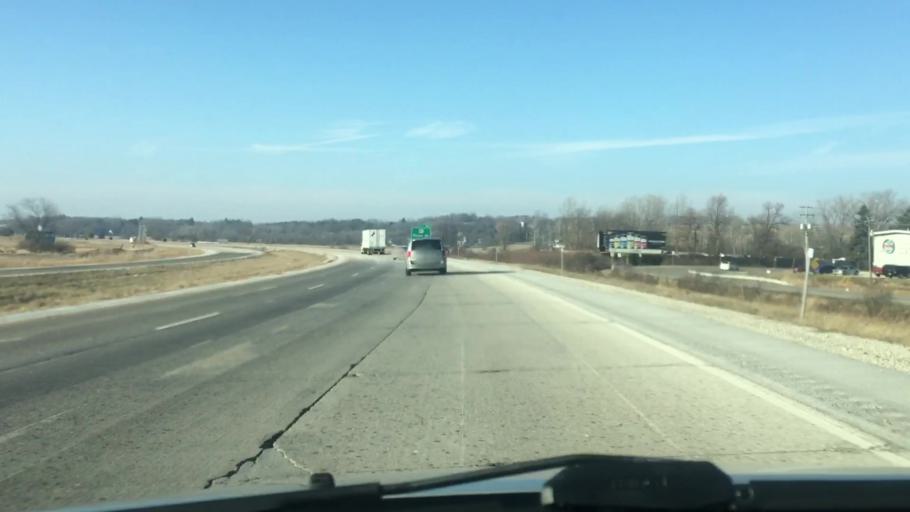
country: US
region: Wisconsin
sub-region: Waukesha County
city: Pewaukee
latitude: 43.0894
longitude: -88.2535
